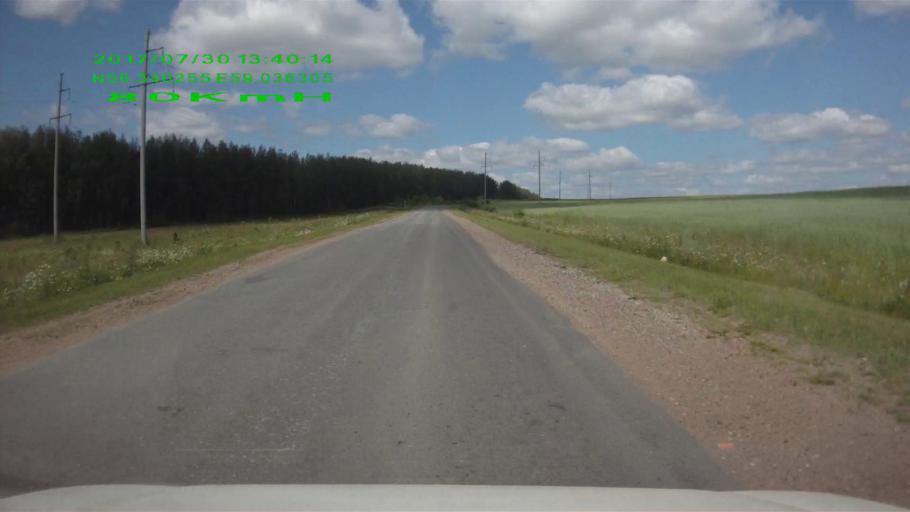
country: RU
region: Sverdlovsk
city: Mikhaylovsk
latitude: 56.3406
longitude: 59.0362
